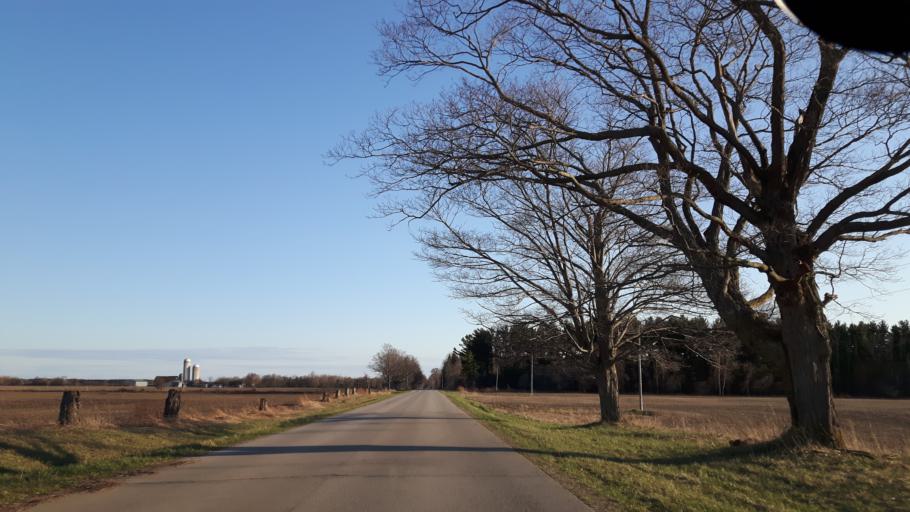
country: CA
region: Ontario
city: Goderich
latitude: 43.6373
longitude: -81.6847
